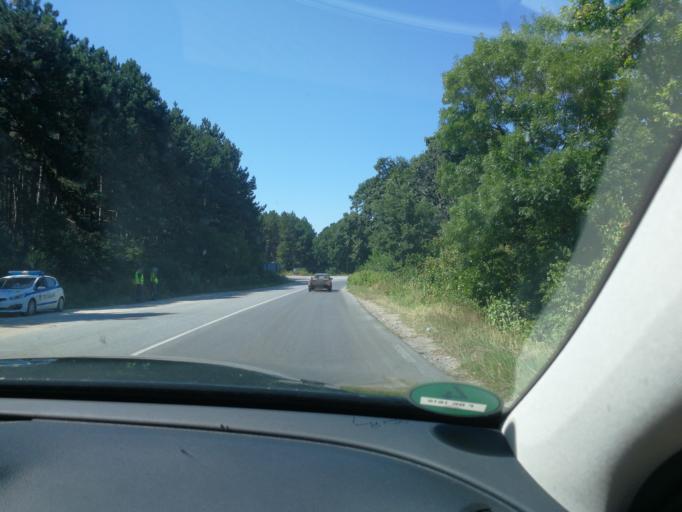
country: BG
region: Khaskovo
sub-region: Obshtina Topolovgrad
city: Topolovgrad
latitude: 42.0781
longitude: 26.3254
